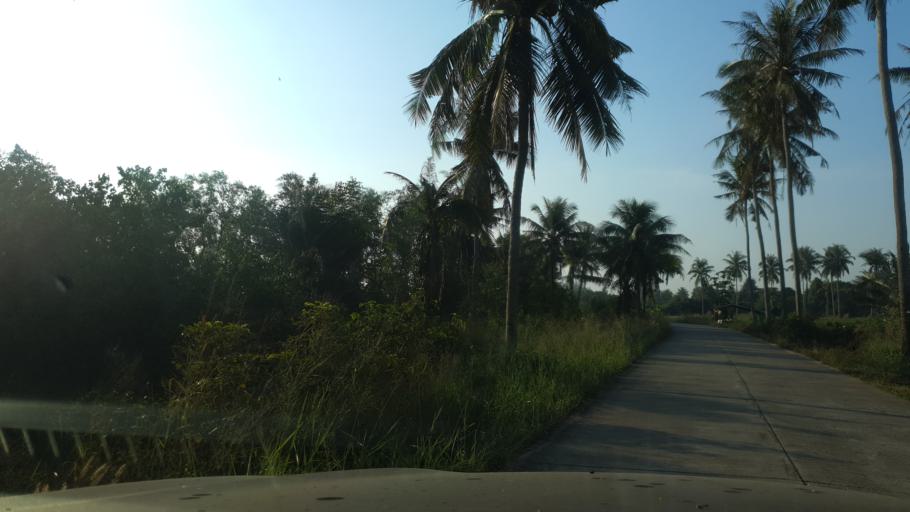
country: TH
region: Prachuap Khiri Khan
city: Bang Saphan
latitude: 11.2943
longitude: 99.5493
